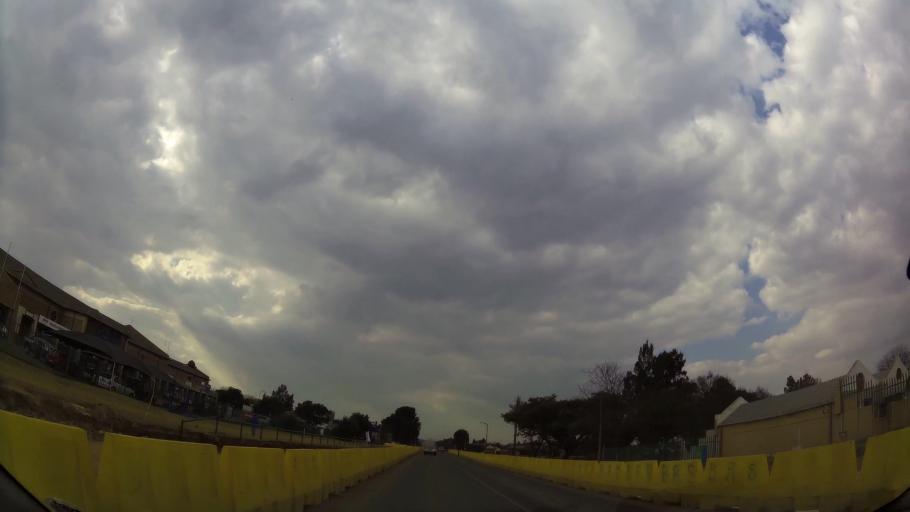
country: ZA
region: Gauteng
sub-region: Ekurhuleni Metropolitan Municipality
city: Benoni
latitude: -26.1459
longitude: 28.3426
